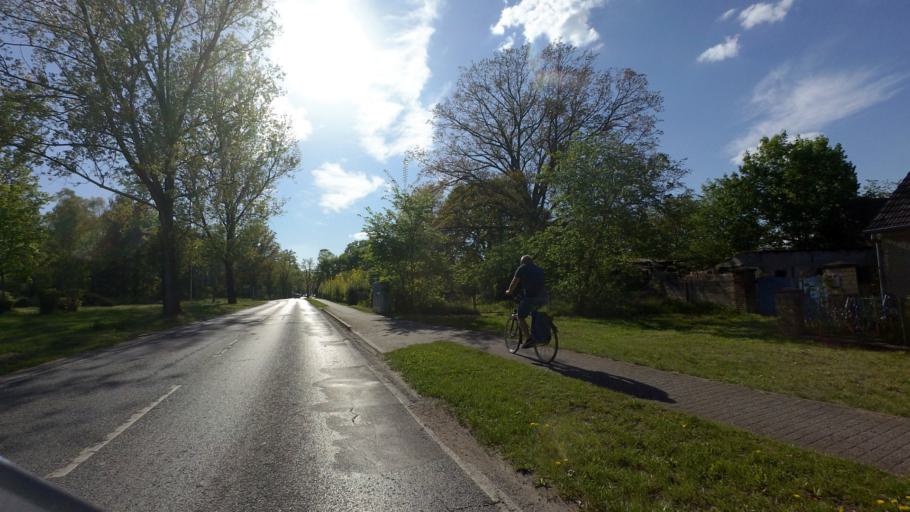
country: DE
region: Brandenburg
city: Oranienburg
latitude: 52.7682
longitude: 13.3248
